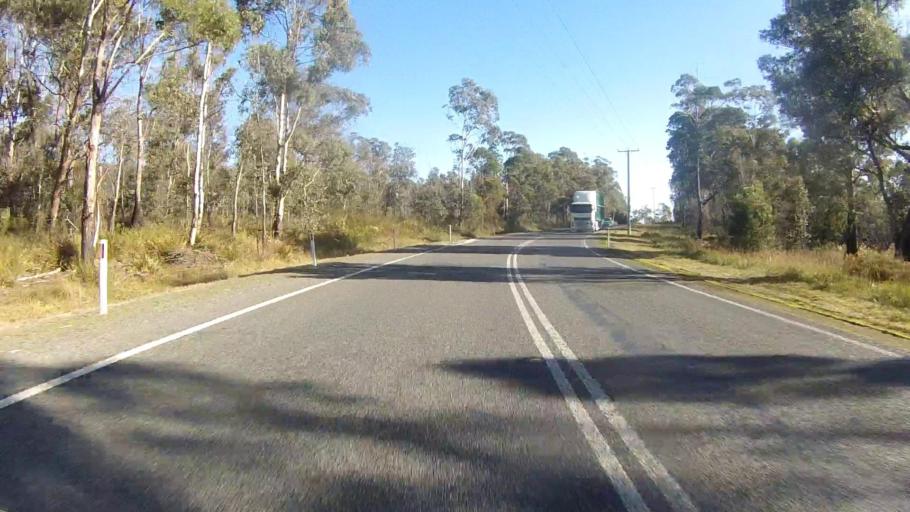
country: AU
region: Tasmania
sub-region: Clarence
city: Sandford
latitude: -43.0239
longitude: 147.8902
